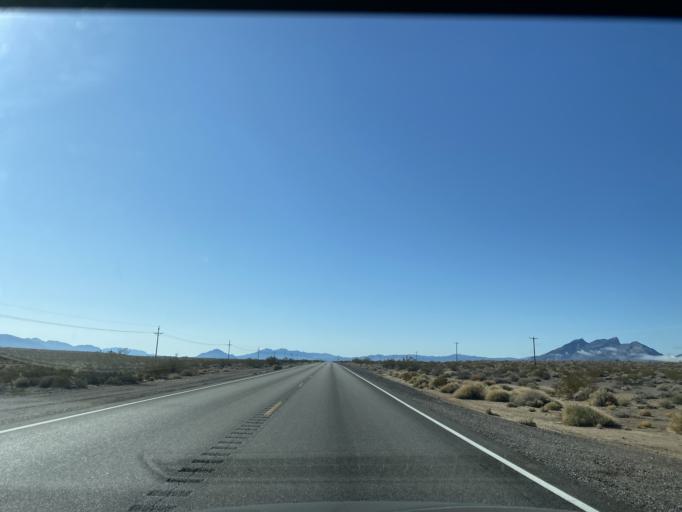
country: US
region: Nevada
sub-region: Nye County
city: Pahrump
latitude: 36.4714
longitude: -116.4217
